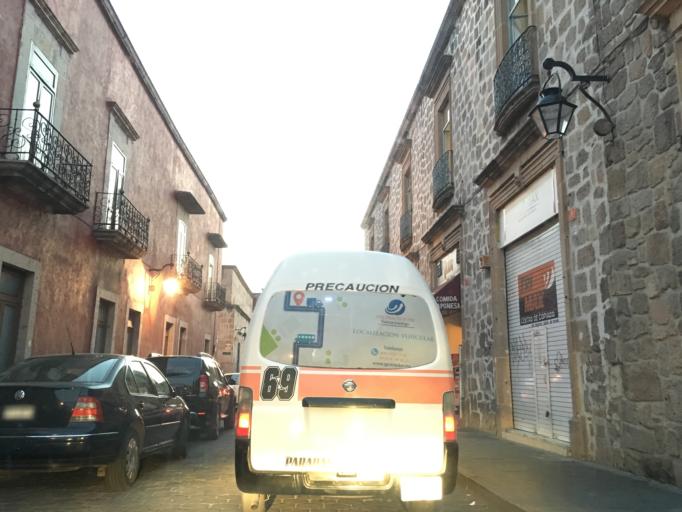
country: MX
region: Michoacan
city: Morelia
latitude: 19.7039
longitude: -101.1910
